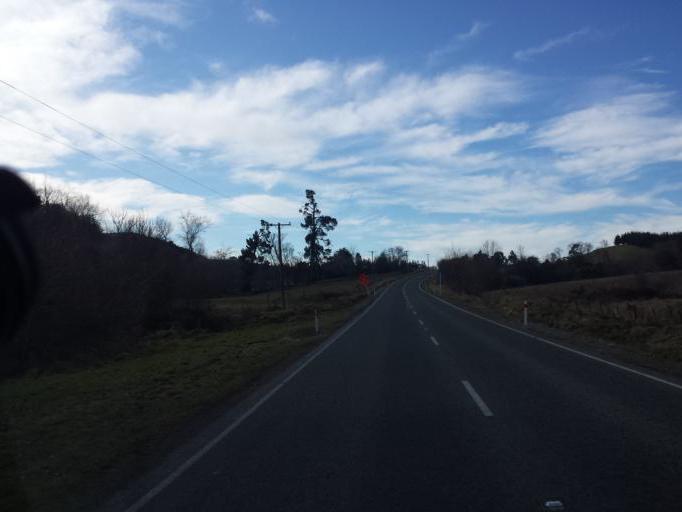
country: NZ
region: Canterbury
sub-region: Timaru District
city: Pleasant Point
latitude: -44.1284
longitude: 171.0908
